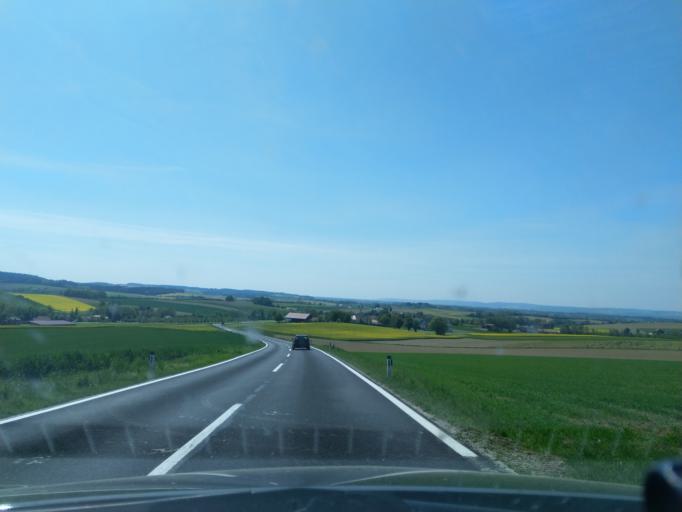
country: DE
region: Bavaria
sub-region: Lower Bavaria
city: Bad Fussing
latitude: 48.2773
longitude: 13.3892
